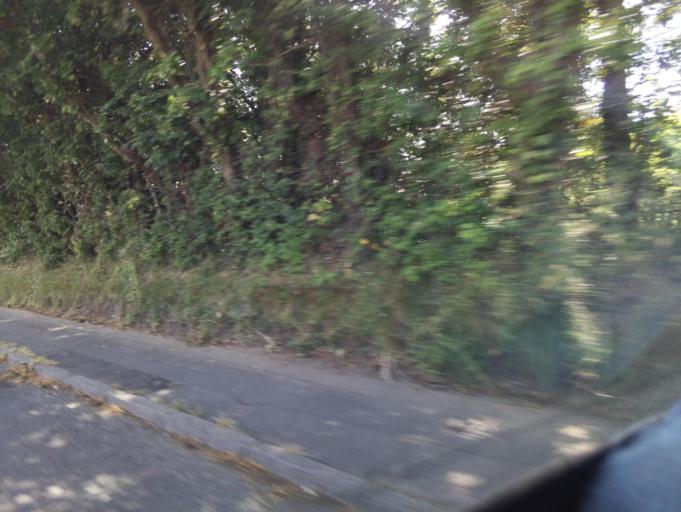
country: GB
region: Wales
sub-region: Caerphilly County Borough
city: Caerphilly
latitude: 51.5719
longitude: -3.2321
